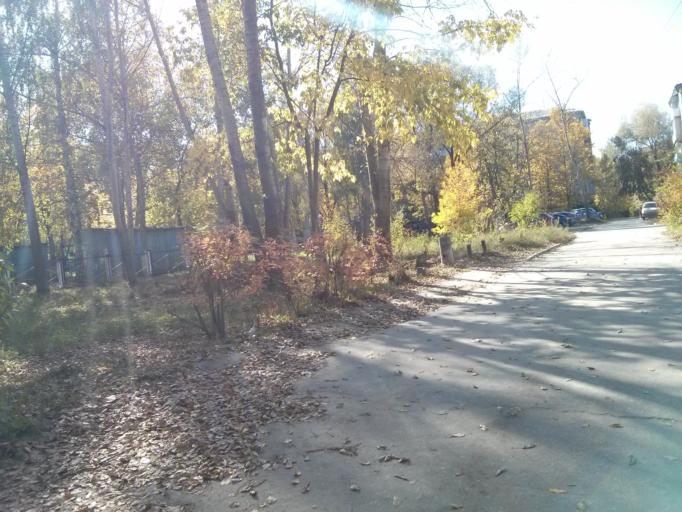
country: RU
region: Vladimir
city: Murom
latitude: 55.5483
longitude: 42.0572
